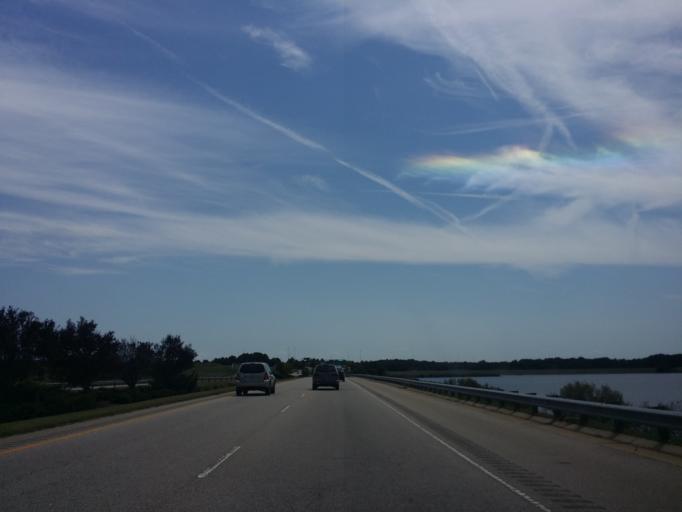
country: US
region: North Carolina
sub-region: Wake County
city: Morrisville
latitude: 35.8769
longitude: -78.8075
